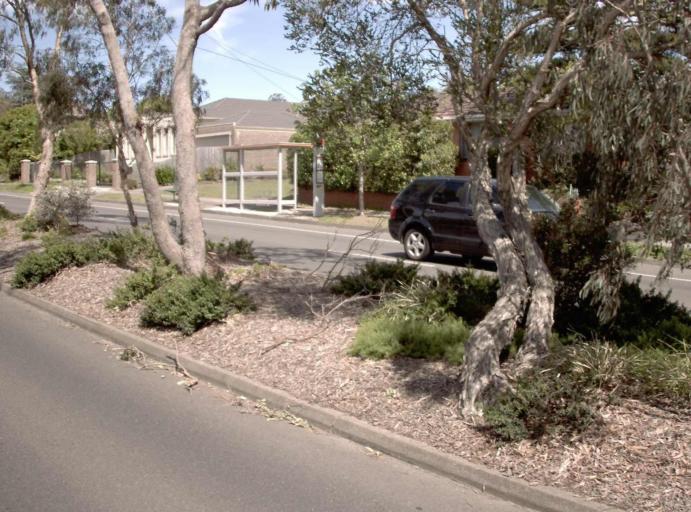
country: AU
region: Victoria
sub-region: Whitehorse
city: Blackburn South
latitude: -37.8367
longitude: 145.1562
